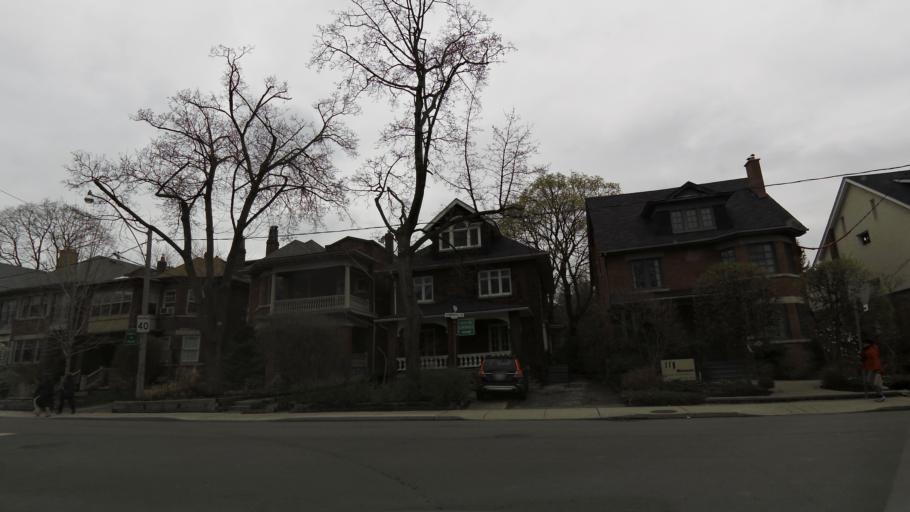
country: CA
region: Ontario
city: Toronto
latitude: 43.6866
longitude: -79.3732
